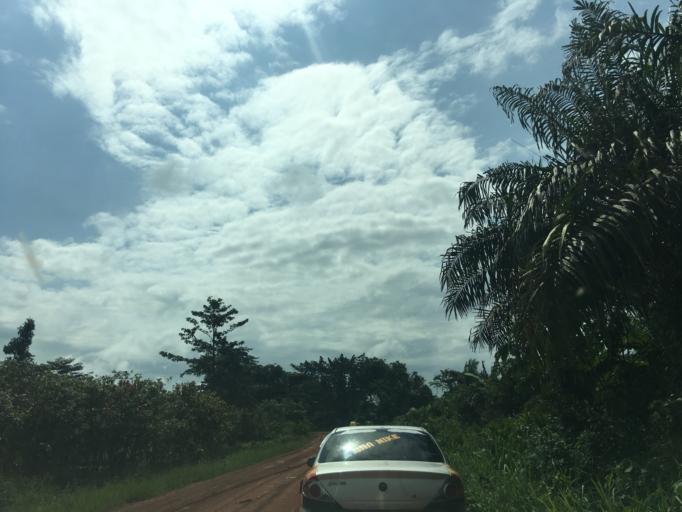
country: GH
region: Western
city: Wassa-Akropong
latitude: 5.7883
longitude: -2.3863
